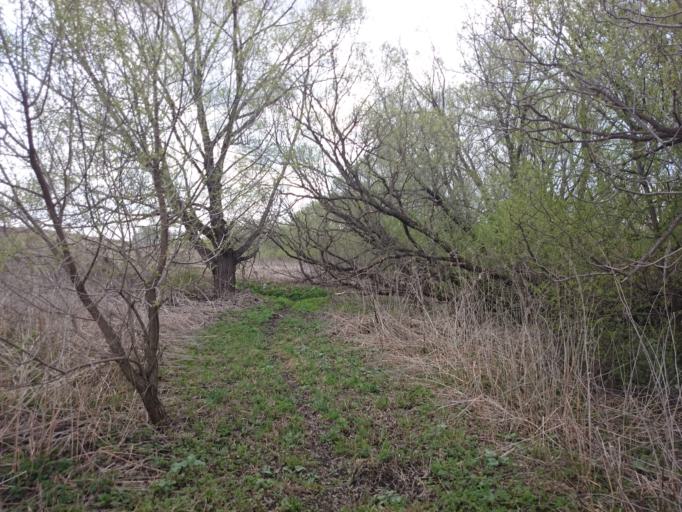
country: RU
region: Mordoviya
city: Kadoshkino
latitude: 54.0318
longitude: 44.4945
